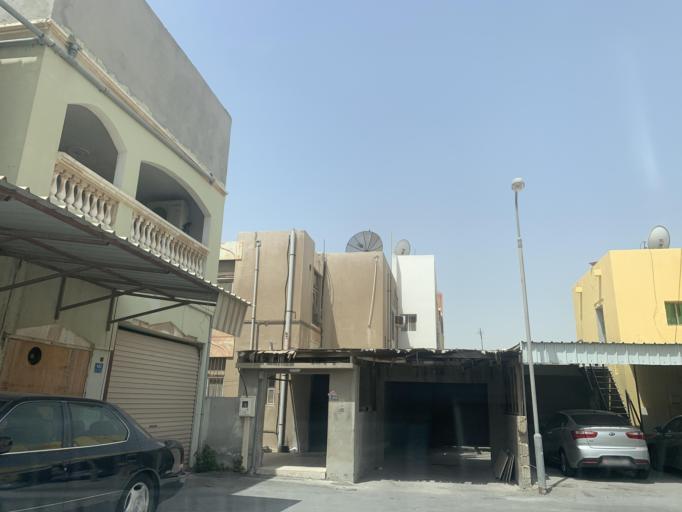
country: BH
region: Northern
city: Madinat `Isa
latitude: 26.1503
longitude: 50.5248
